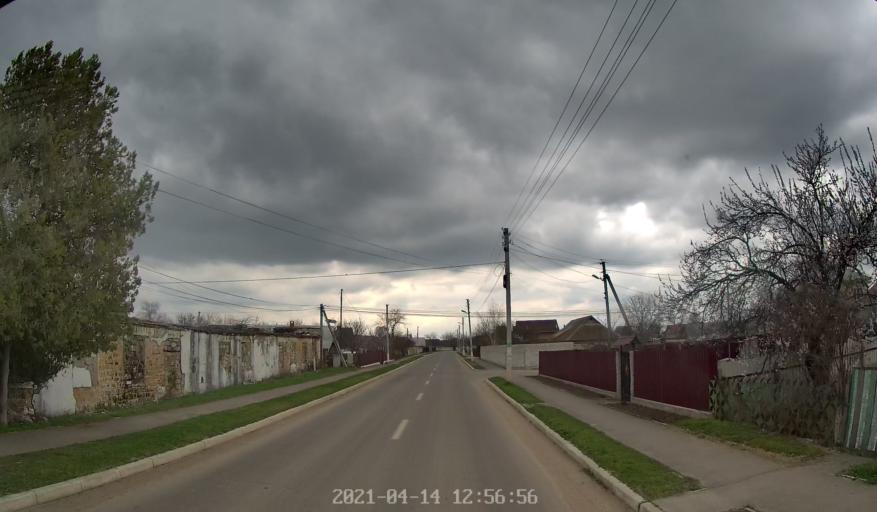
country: MD
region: Criuleni
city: Criuleni
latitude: 47.1530
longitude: 29.1454
